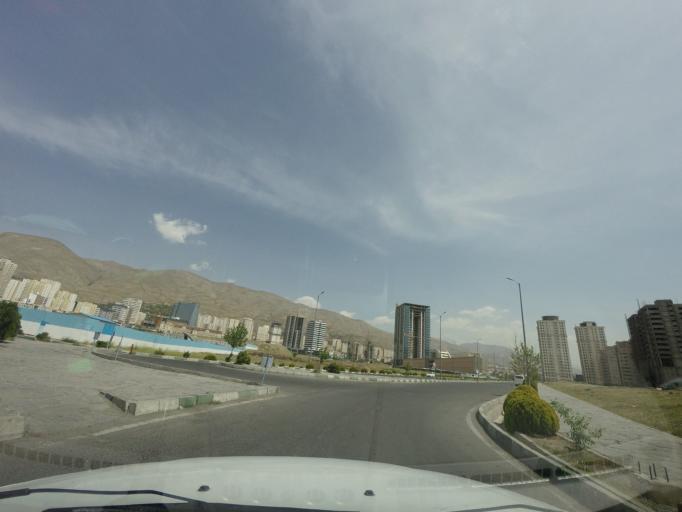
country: IR
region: Tehran
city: Shahr-e Qods
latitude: 35.7475
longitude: 51.2222
